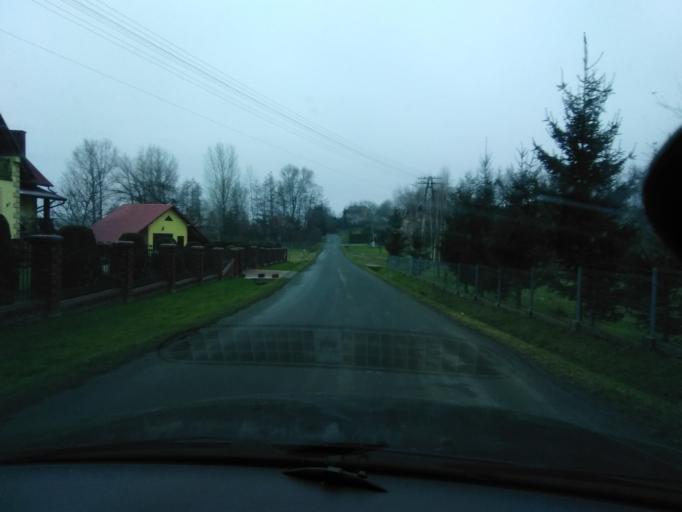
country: PL
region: Subcarpathian Voivodeship
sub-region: Powiat przeworski
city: Zarzecze
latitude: 49.9613
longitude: 22.5677
